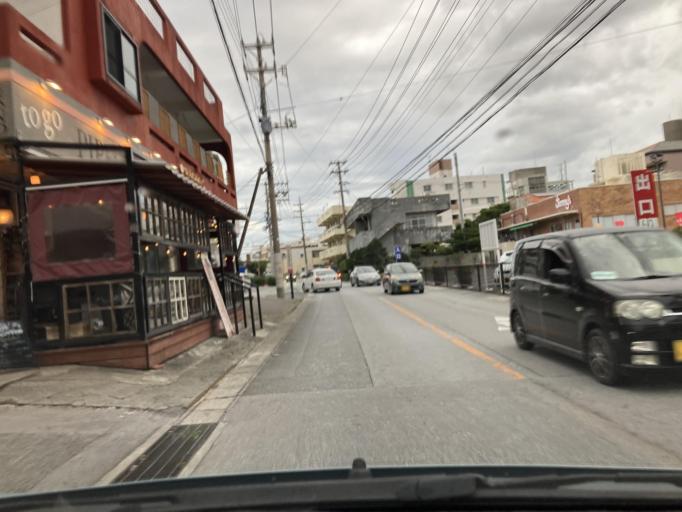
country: JP
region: Okinawa
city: Ginowan
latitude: 26.2750
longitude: 127.7424
